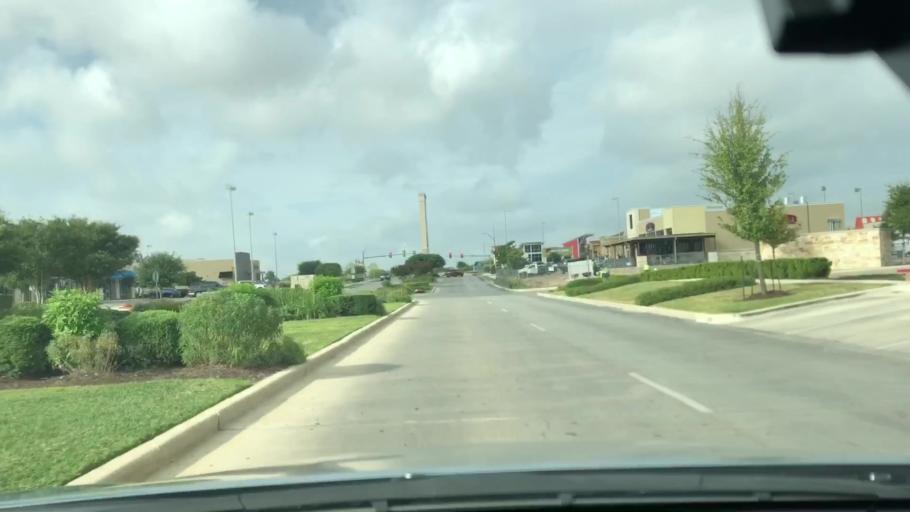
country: US
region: Texas
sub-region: Guadalupe County
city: Lake Dunlap
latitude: 29.7284
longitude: -98.0742
